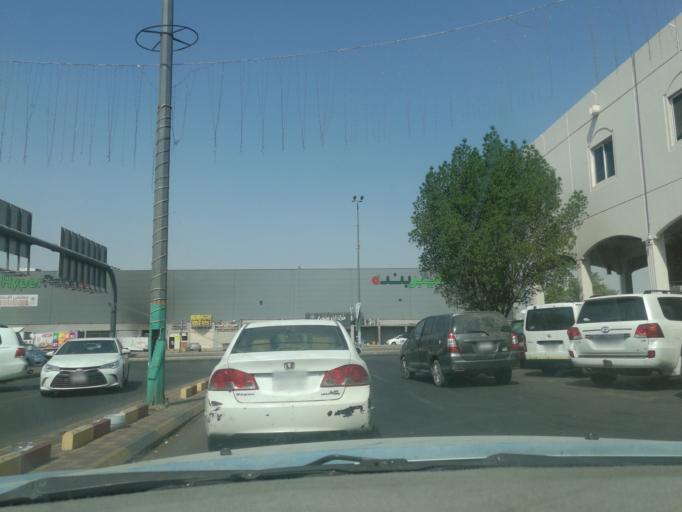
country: SA
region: Makkah
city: Mecca
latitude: 21.3688
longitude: 39.8046
